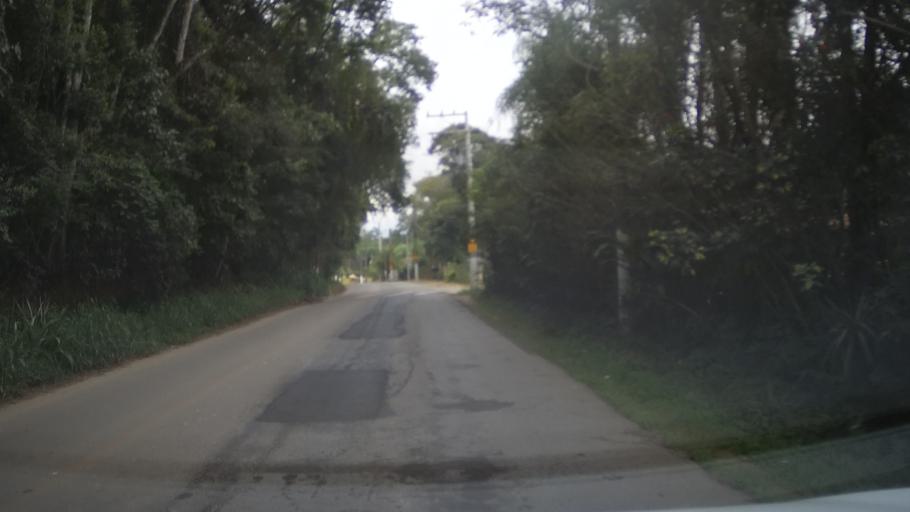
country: BR
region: Sao Paulo
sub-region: Aruja
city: Aruja
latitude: -23.3897
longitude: -46.3420
